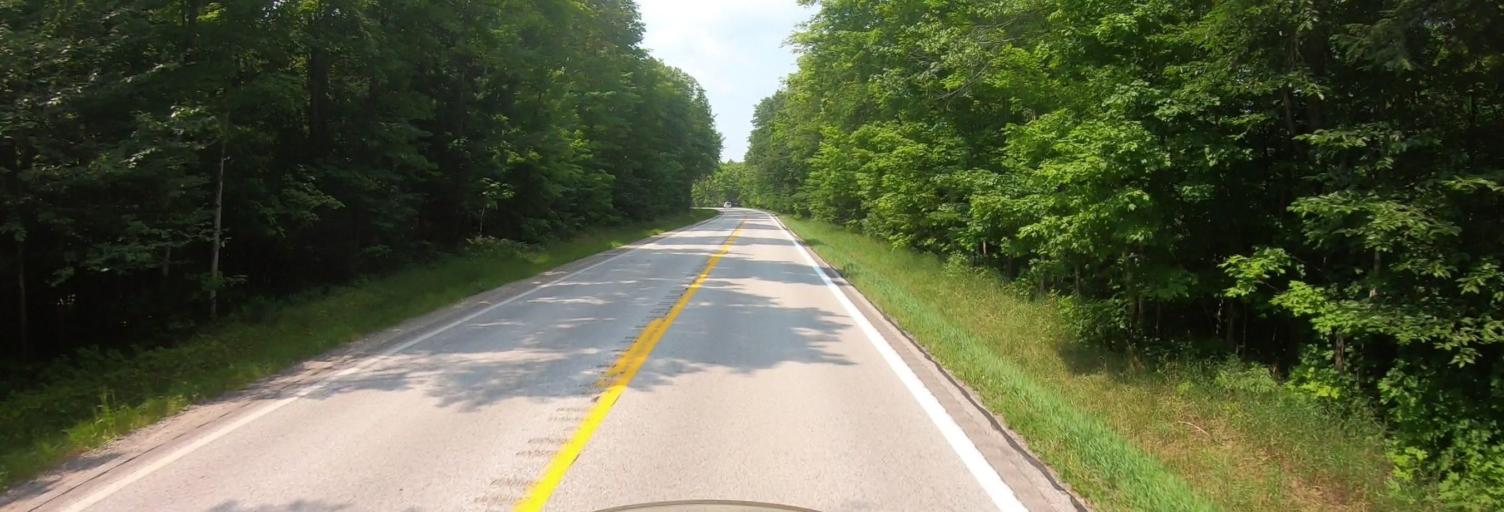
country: US
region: Michigan
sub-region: Luce County
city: Newberry
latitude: 46.5162
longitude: -85.4221
